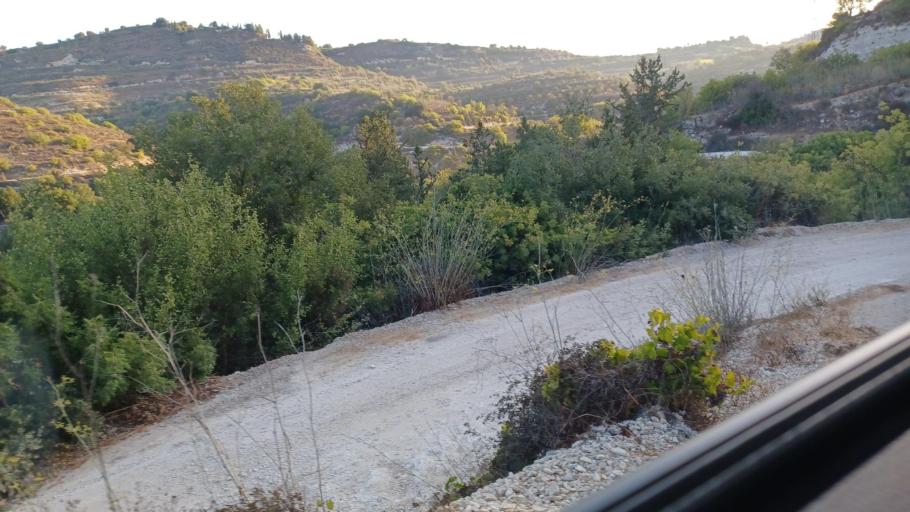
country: CY
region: Pafos
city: Tala
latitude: 34.8705
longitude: 32.4703
